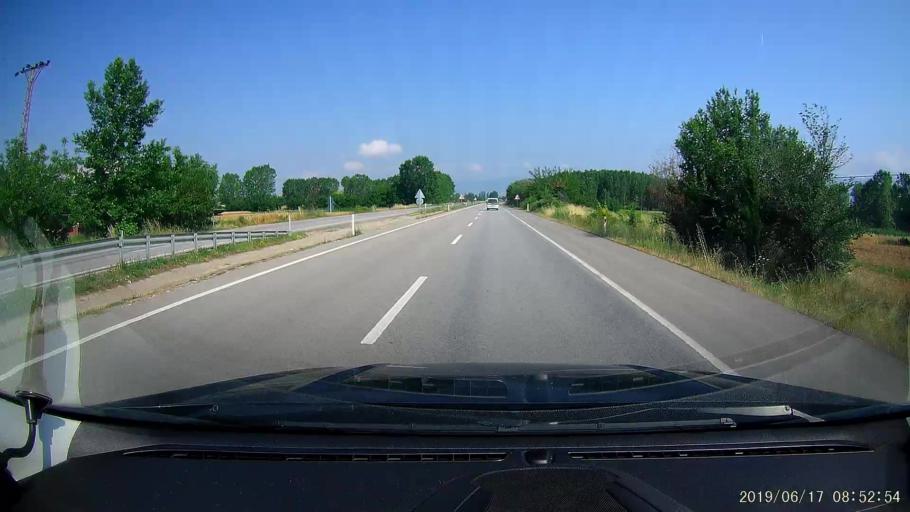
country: TR
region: Tokat
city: Erbaa
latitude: 40.7038
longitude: 36.4894
